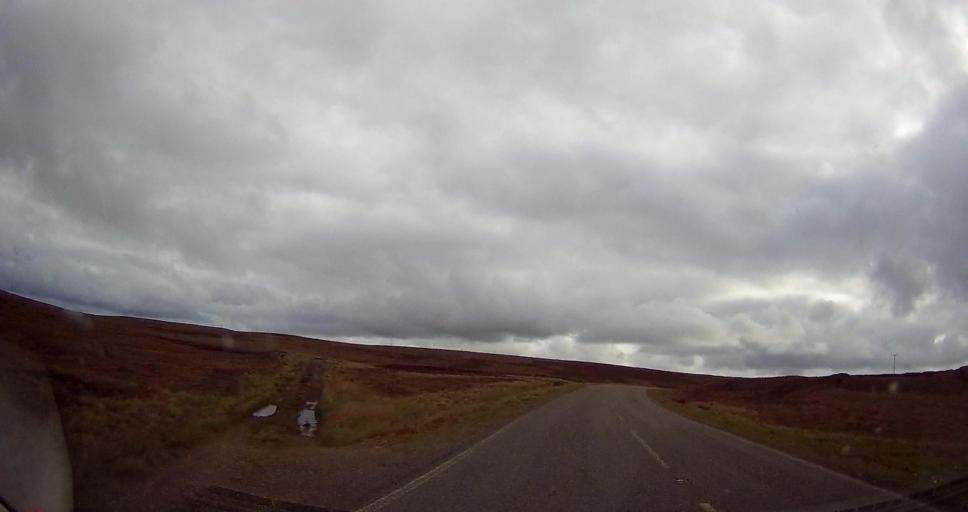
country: GB
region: Scotland
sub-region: Shetland Islands
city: Shetland
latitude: 60.6648
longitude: -1.0363
